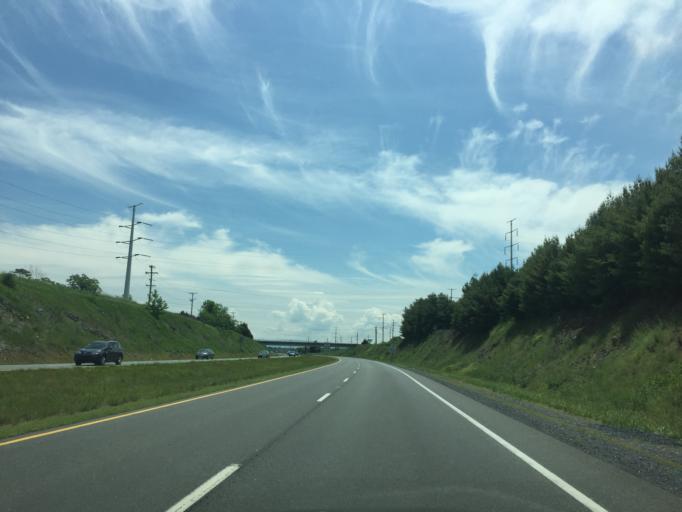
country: US
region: Virginia
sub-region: Frederick County
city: Stephens City
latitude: 39.1309
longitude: -78.2067
